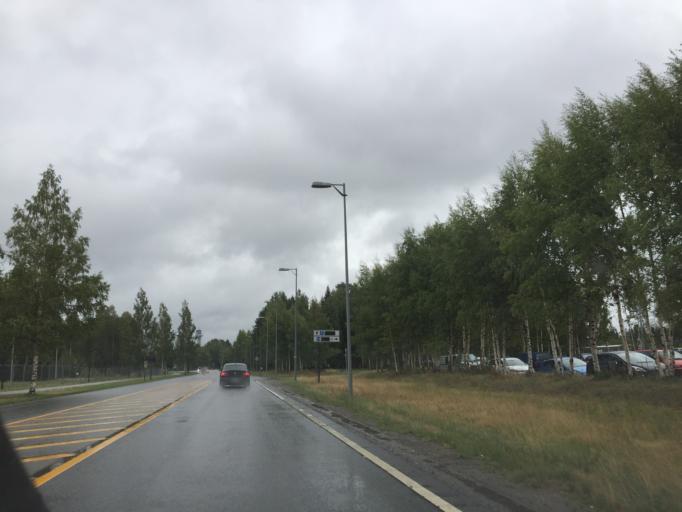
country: NO
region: Akershus
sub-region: Nannestad
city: Teigebyen
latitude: 60.1817
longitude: 11.0856
